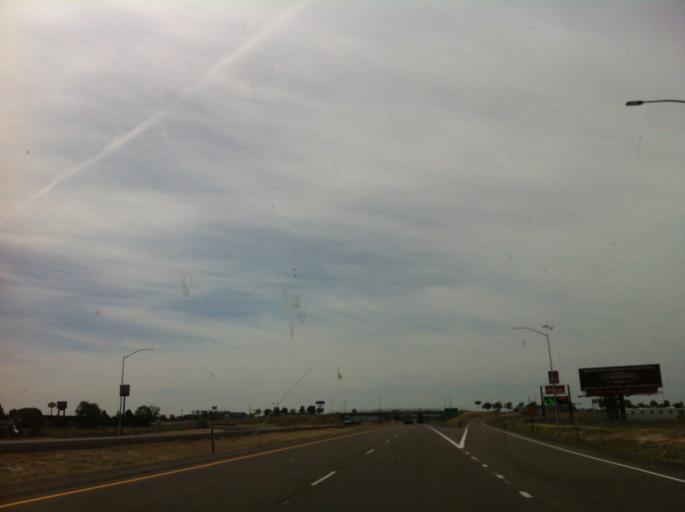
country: US
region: Oregon
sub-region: Malheur County
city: Ontario
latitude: 44.0338
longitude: -116.9547
